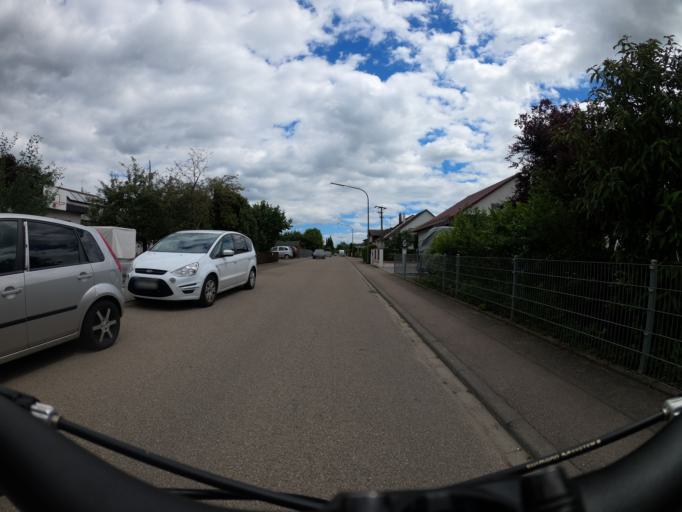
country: DE
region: Bavaria
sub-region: Swabia
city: Nersingen
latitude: 48.4336
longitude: 10.1136
